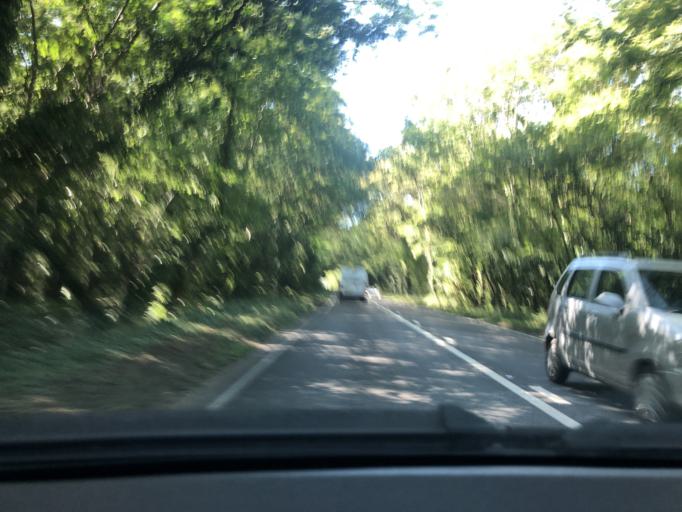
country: GB
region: England
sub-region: Somerset
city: Westonzoyland
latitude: 51.1347
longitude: -2.8544
